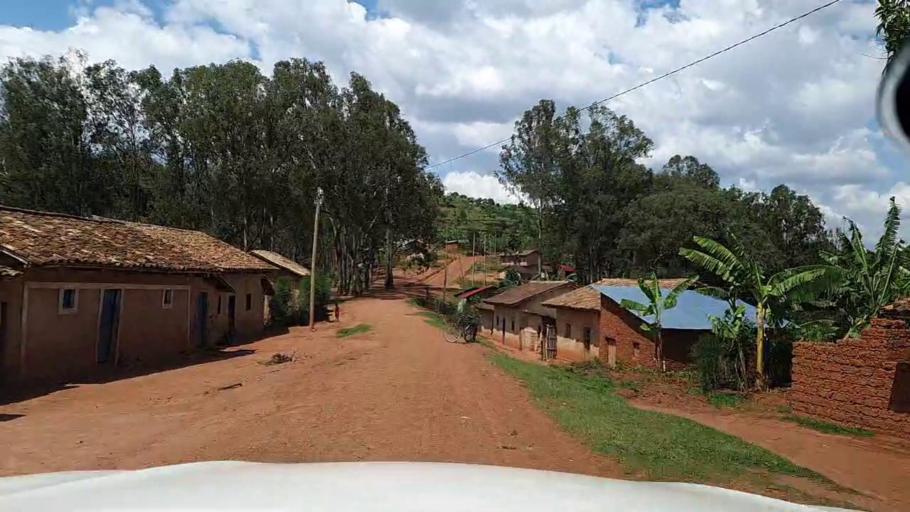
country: RW
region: Southern Province
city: Butare
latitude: -2.7504
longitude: 29.7025
